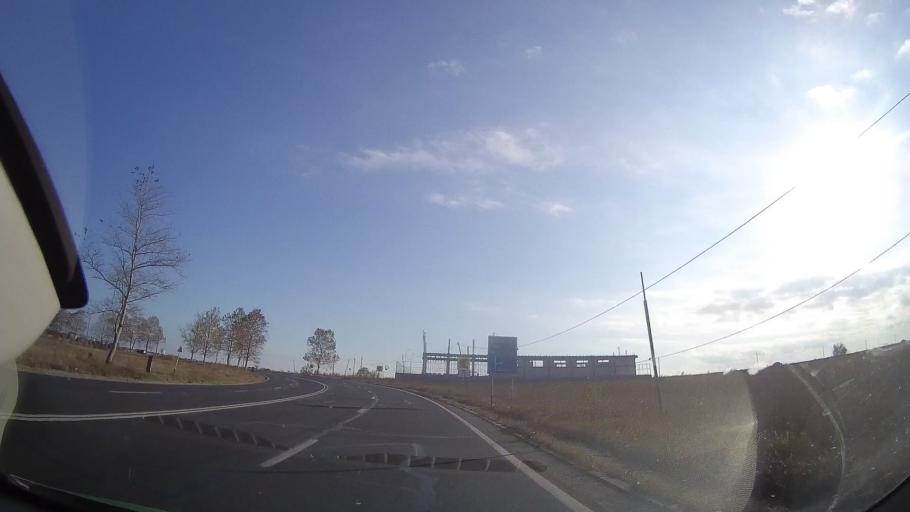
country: RO
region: Constanta
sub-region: Municipiul Mangalia
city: Mangalia
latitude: 43.7943
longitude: 28.5606
